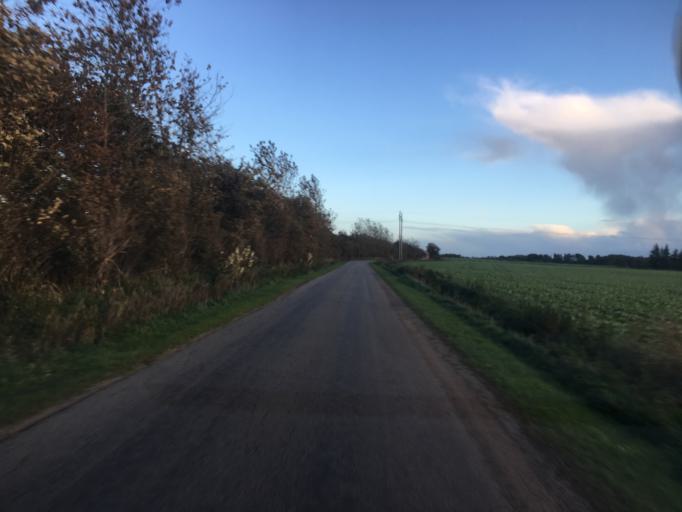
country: DE
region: Schleswig-Holstein
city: Ellhoft
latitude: 54.9559
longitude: 9.0178
